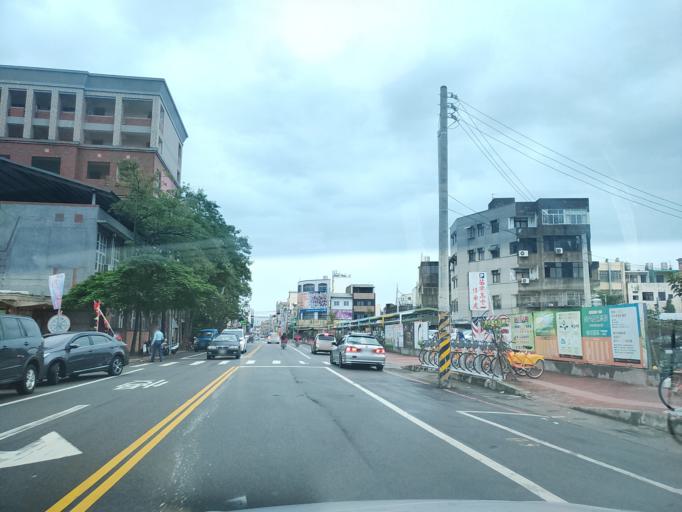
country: TW
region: Taiwan
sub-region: Miaoli
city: Miaoli
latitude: 24.5586
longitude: 120.8163
